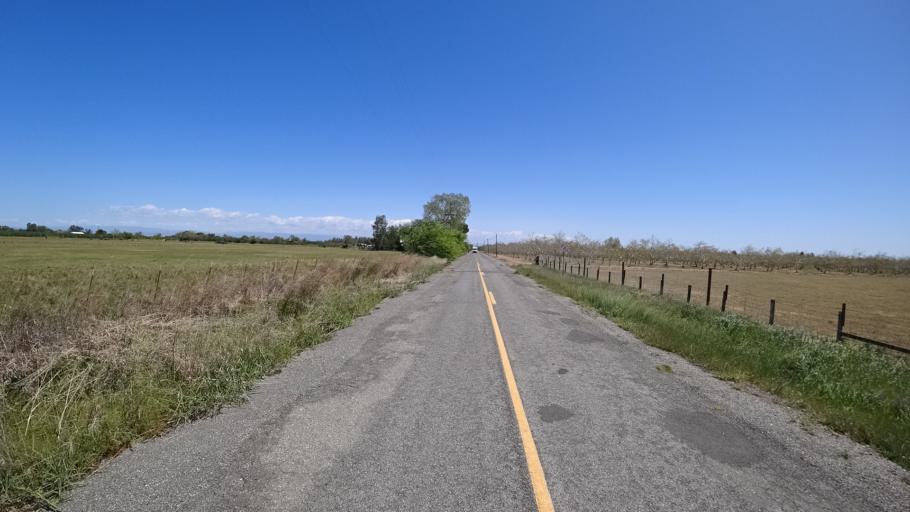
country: US
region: California
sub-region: Glenn County
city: Orland
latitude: 39.7894
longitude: -122.2145
